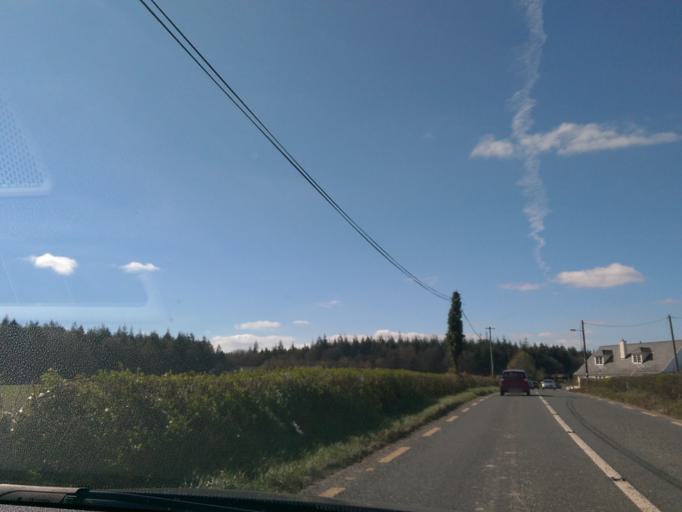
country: IE
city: Ballylinan
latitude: 53.0035
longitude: -7.0717
